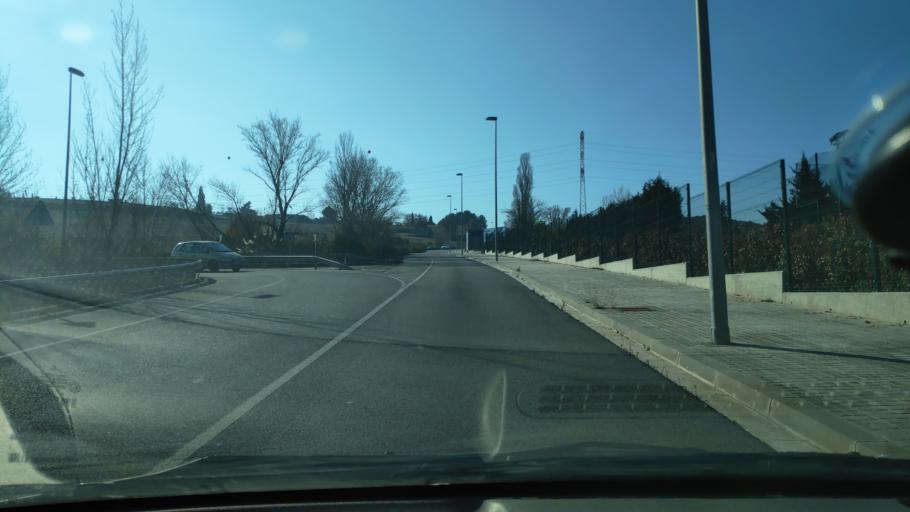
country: ES
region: Catalonia
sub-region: Provincia de Barcelona
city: Sant Quirze del Valles
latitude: 41.5132
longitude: 2.0972
